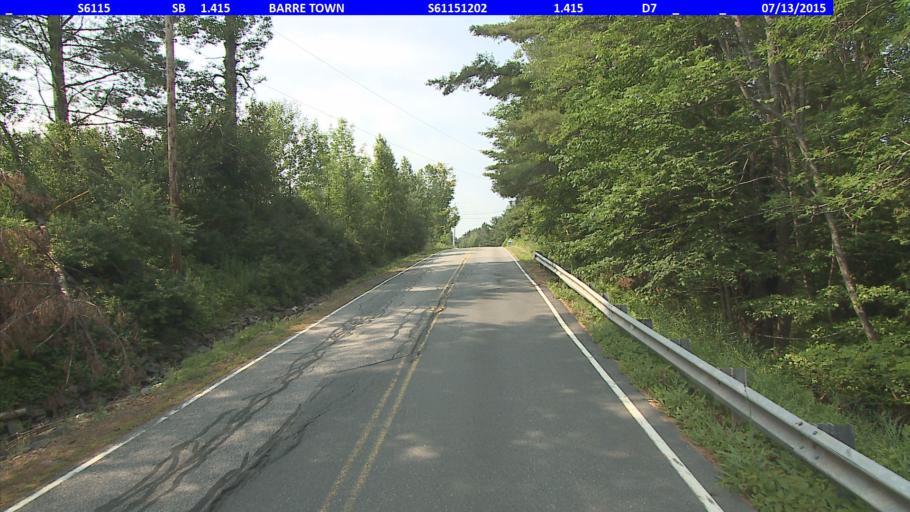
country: US
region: Vermont
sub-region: Washington County
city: Barre
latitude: 44.2179
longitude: -72.4735
